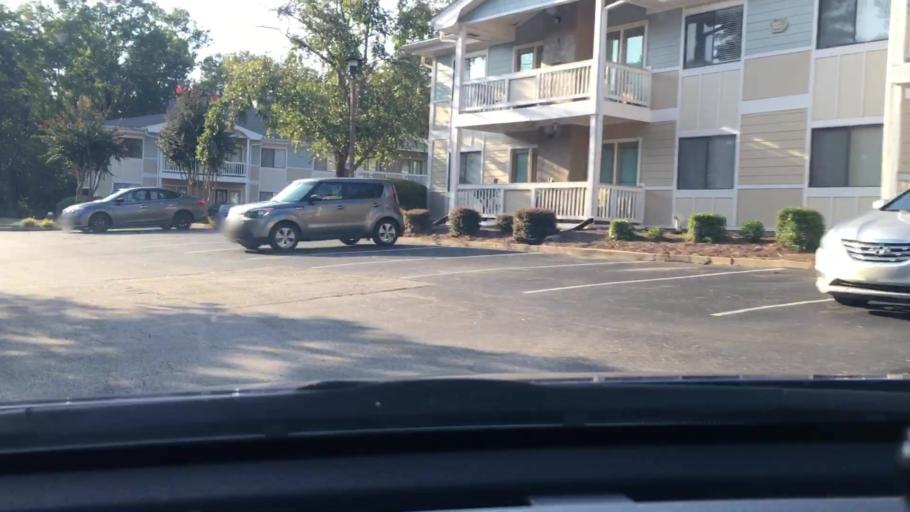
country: US
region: South Carolina
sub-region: Lexington County
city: Seven Oaks
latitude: 34.0828
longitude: -81.1459
